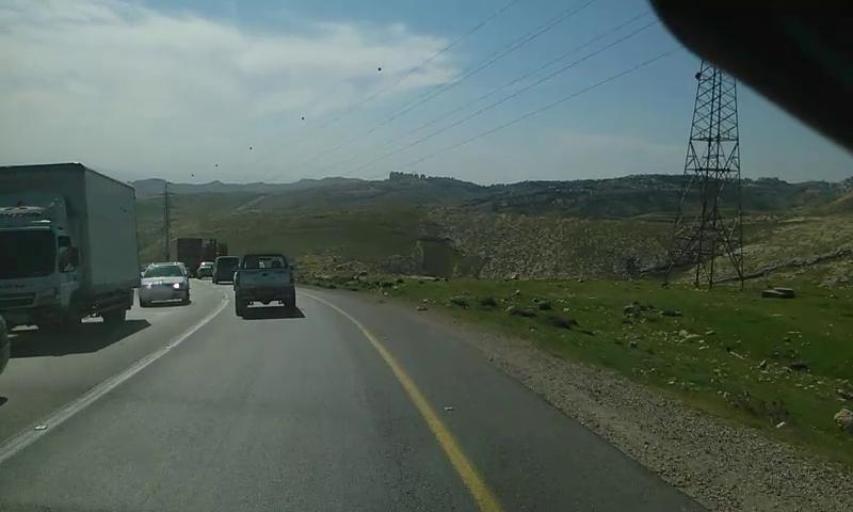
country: PS
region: West Bank
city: `Anata
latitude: 31.8137
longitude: 35.2966
